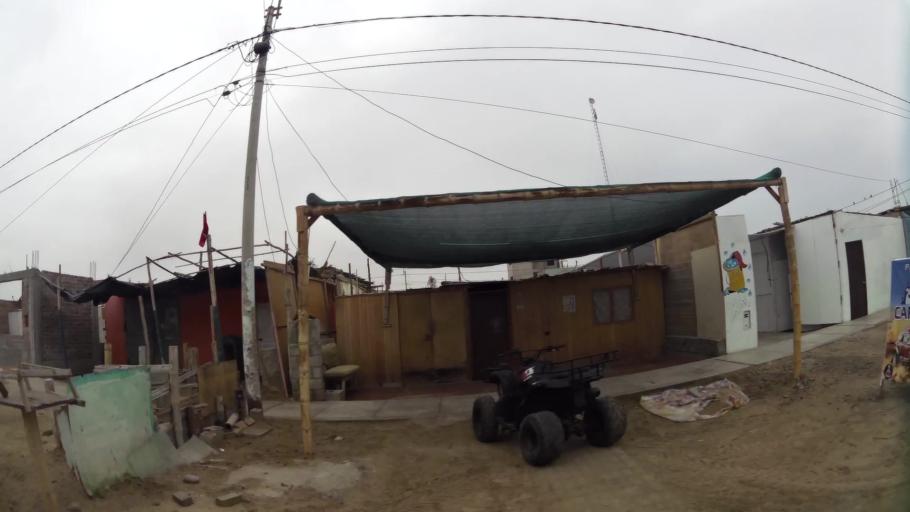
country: PE
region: Ica
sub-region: Provincia de Pisco
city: Paracas
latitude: -13.8375
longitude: -76.2483
